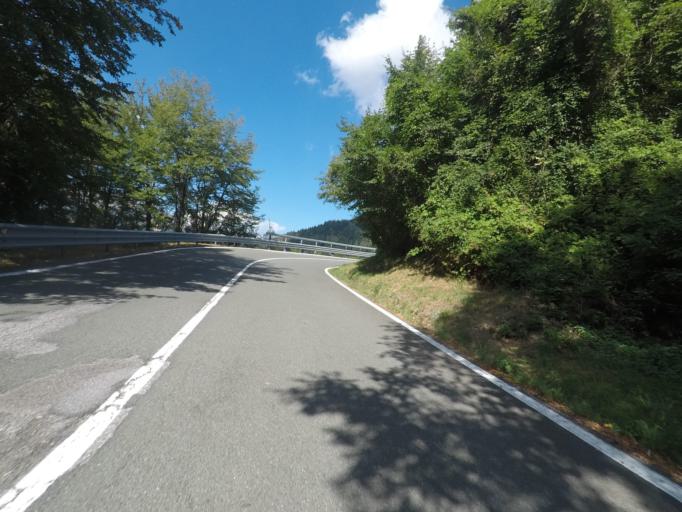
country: IT
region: Tuscany
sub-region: Provincia di Massa-Carrara
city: Comano
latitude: 44.2650
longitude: 10.1725
